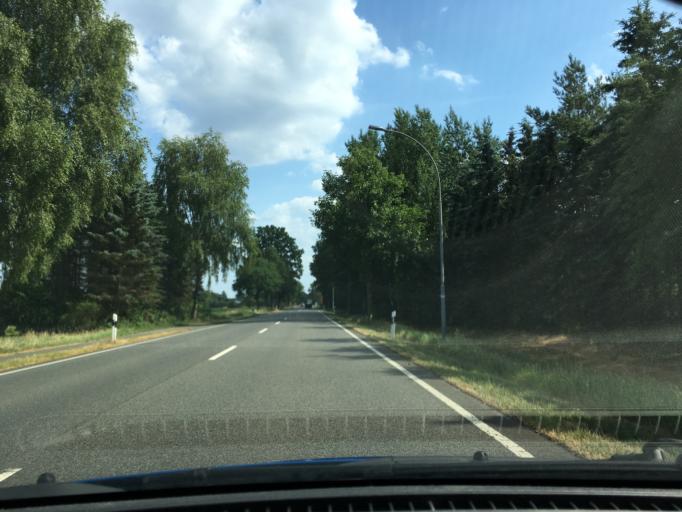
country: DE
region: Lower Saxony
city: Handeloh
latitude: 53.1899
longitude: 9.8324
